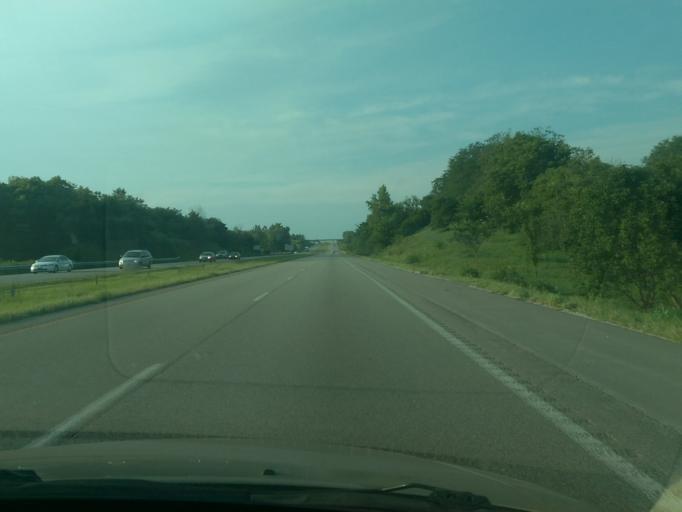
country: US
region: Missouri
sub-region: Platte County
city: Platte City
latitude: 39.4628
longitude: -94.7879
